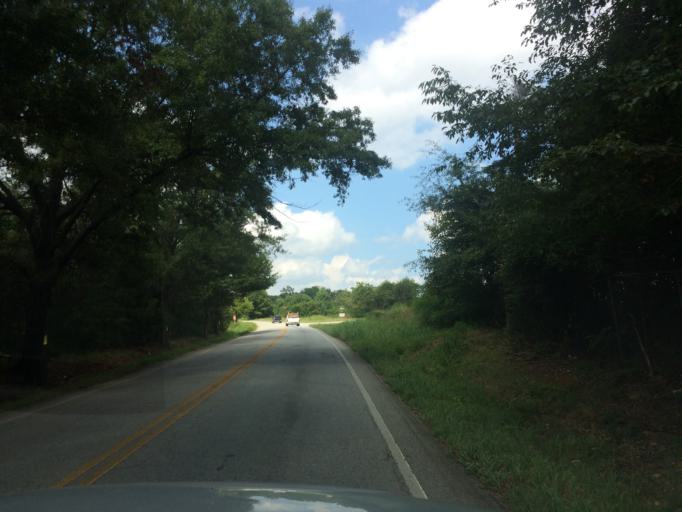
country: US
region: South Carolina
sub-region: Spartanburg County
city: Fairforest
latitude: 34.9402
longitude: -82.0316
